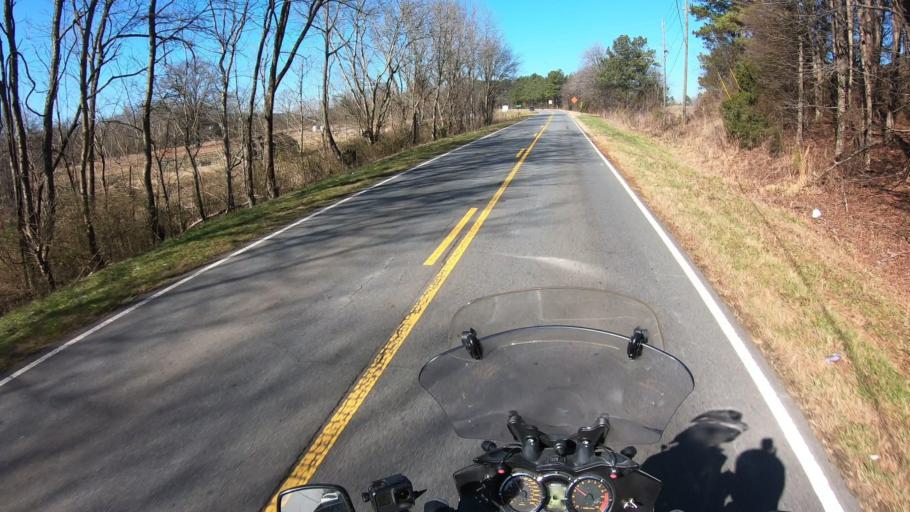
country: US
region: Georgia
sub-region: Bartow County
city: Cartersville
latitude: 34.2682
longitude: -84.8084
